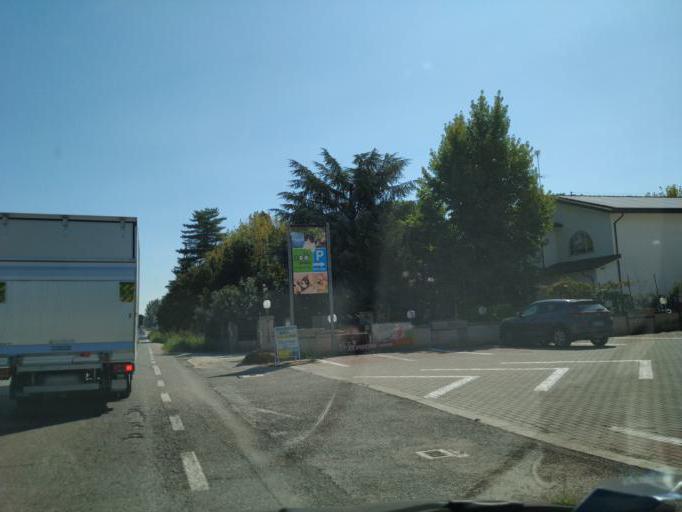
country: IT
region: Emilia-Romagna
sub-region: Provincia di Ferrara
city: Copparo
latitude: 44.8893
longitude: 11.8039
